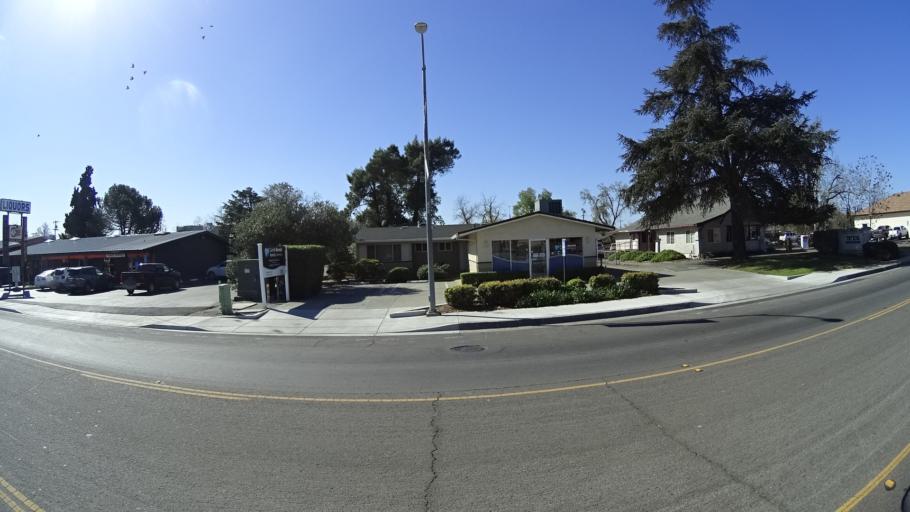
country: US
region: California
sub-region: Glenn County
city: Orland
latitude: 39.7477
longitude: -122.1834
